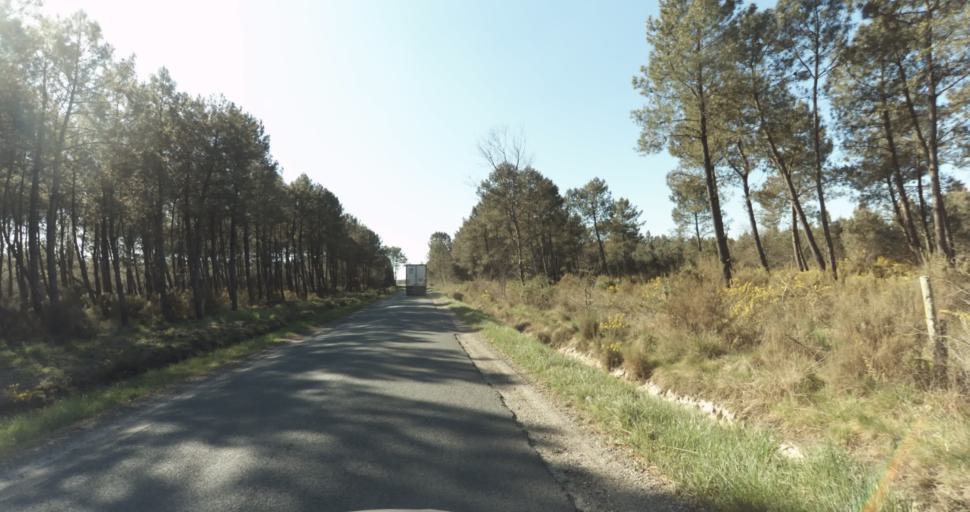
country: FR
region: Aquitaine
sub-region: Departement de la Gironde
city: Marcheprime
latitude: 44.7578
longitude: -0.8513
